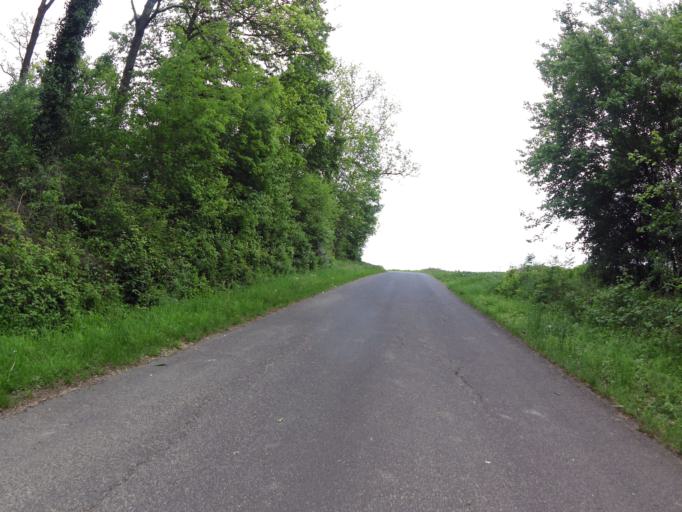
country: DE
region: Bavaria
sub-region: Regierungsbezirk Unterfranken
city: Unterpleichfeld
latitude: 49.8431
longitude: 10.0705
